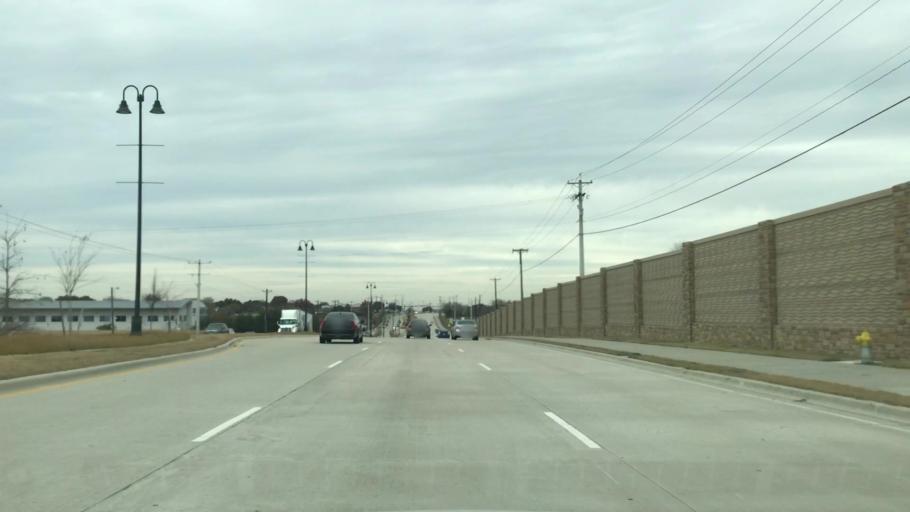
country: US
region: Texas
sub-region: Denton County
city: The Colony
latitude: 33.0891
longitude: -96.8927
